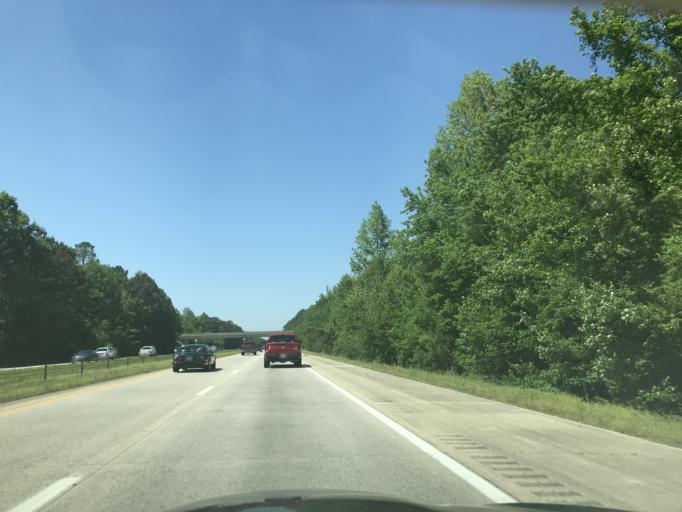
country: US
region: North Carolina
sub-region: Johnston County
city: Benson
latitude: 35.4884
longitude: -78.5519
